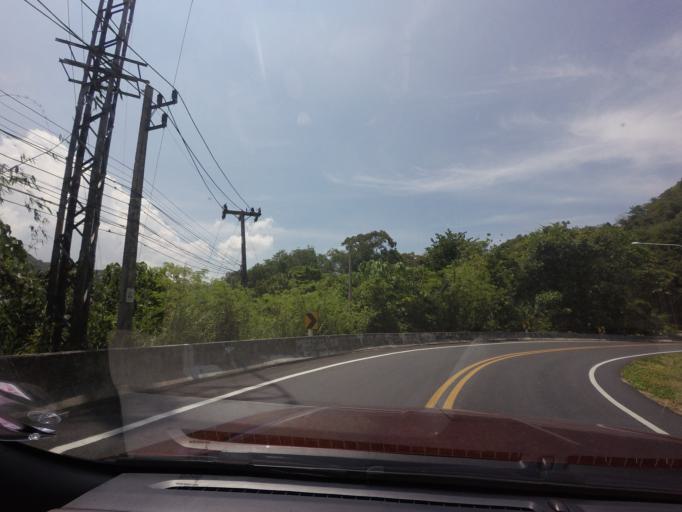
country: TH
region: Yala
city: Betong
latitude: 5.9059
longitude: 101.1486
